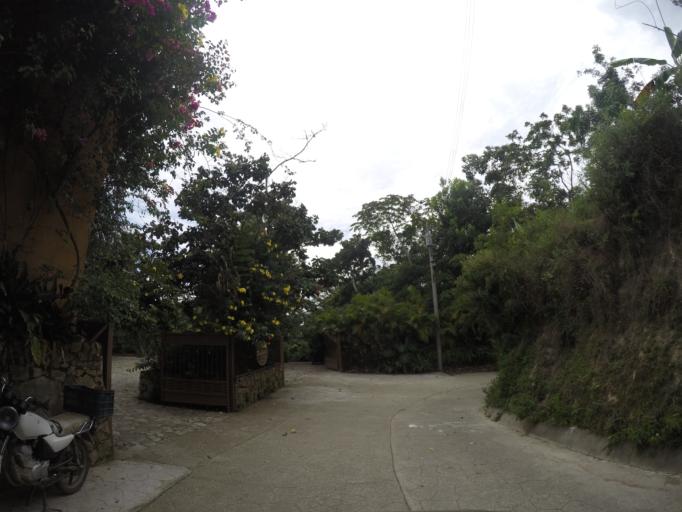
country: MX
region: Oaxaca
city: Pluma Hidalgo
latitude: 15.9141
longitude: -96.4170
